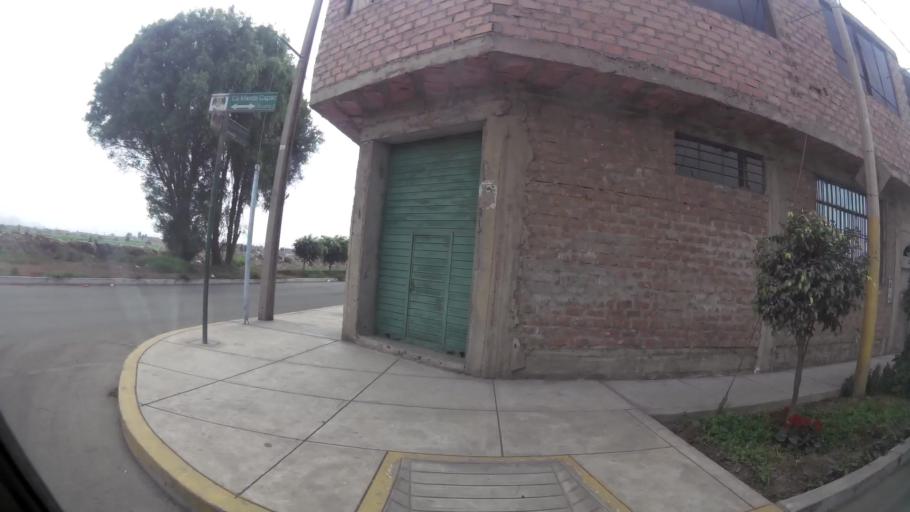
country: PE
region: Lima
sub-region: Provincia de Huaral
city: Huaral
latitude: -11.4952
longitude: -77.2182
